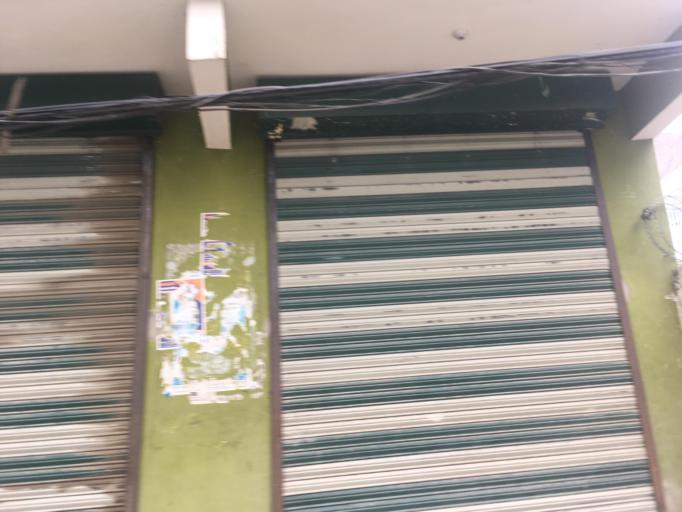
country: PK
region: Gilgit-Baltistan
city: Skardu
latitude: 35.2769
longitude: 75.6370
